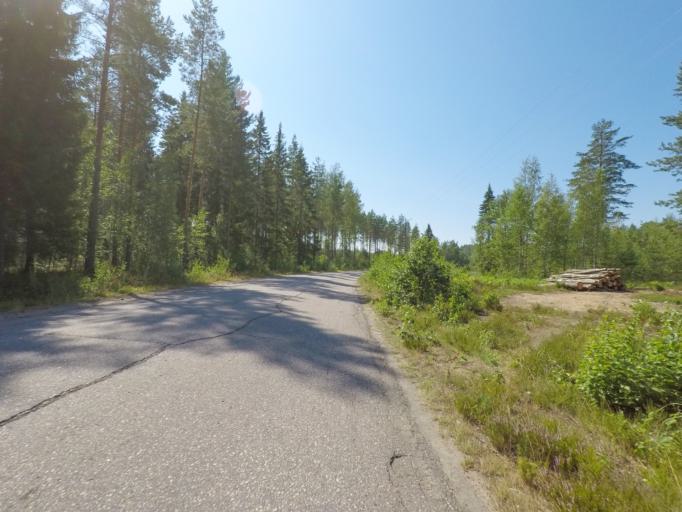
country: FI
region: Southern Savonia
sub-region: Mikkeli
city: Puumala
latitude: 61.4248
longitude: 28.1566
